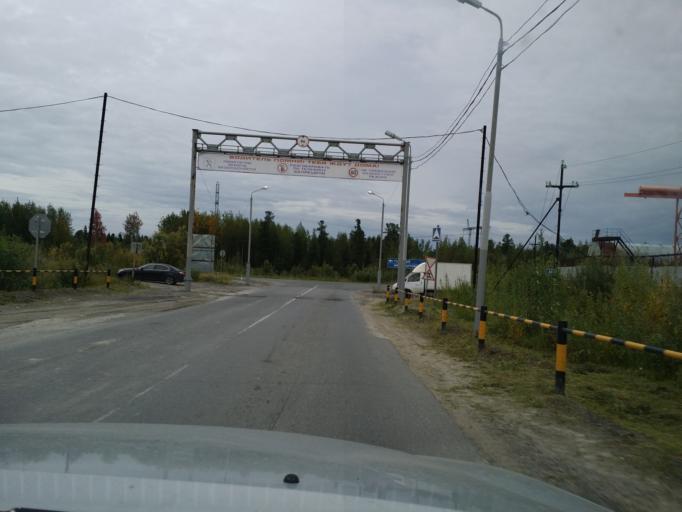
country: RU
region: Khanty-Mansiyskiy Avtonomnyy Okrug
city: Izluchinsk
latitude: 61.1659
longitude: 76.9247
